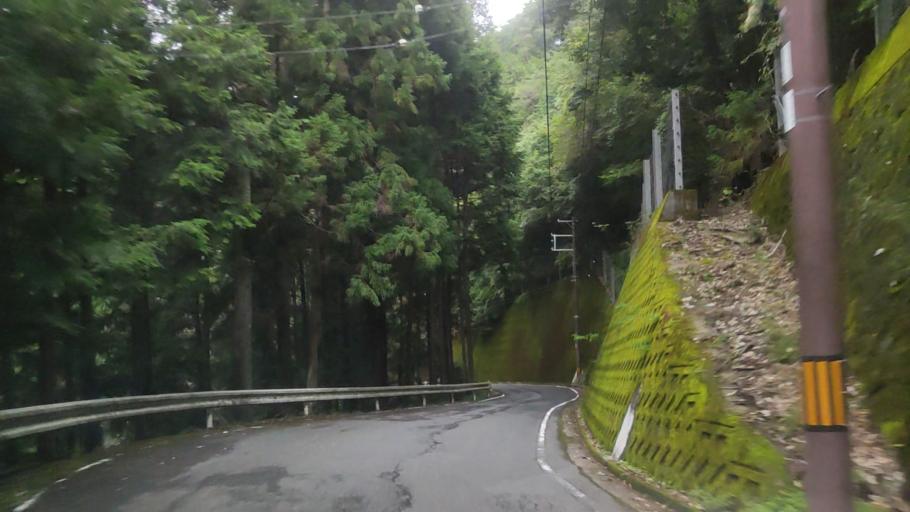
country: JP
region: Wakayama
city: Koya
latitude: 34.2401
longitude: 135.6523
